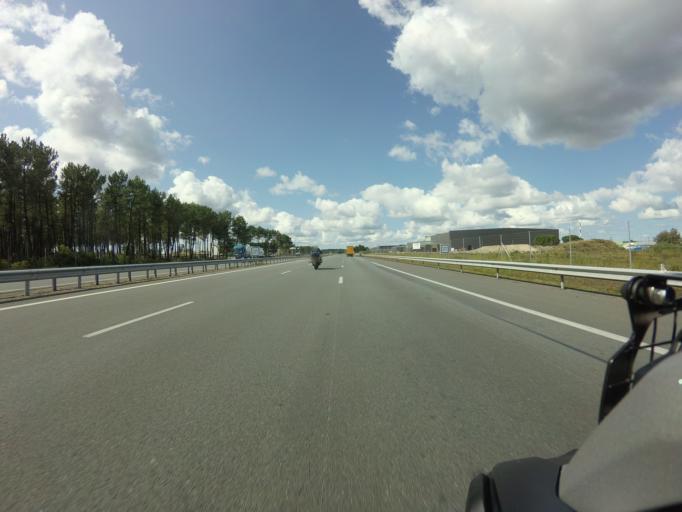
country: FR
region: Aquitaine
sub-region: Departement des Landes
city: Castets
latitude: 43.8703
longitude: -1.1439
